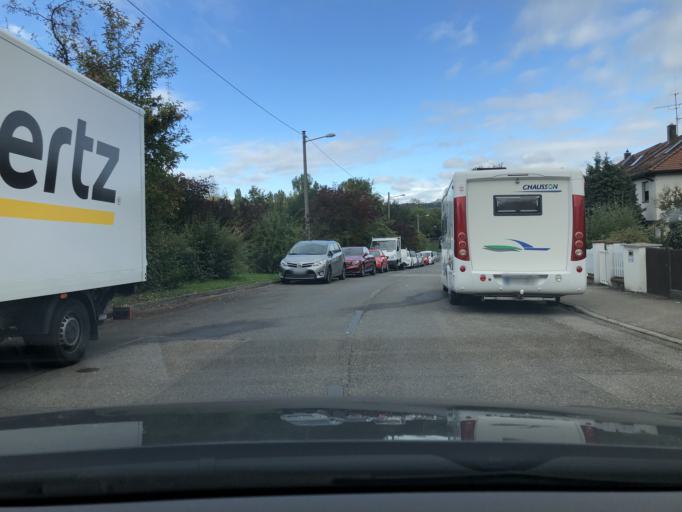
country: DE
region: Baden-Wuerttemberg
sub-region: Regierungsbezirk Stuttgart
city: Stuttgart Muehlhausen
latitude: 48.8239
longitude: 9.2122
